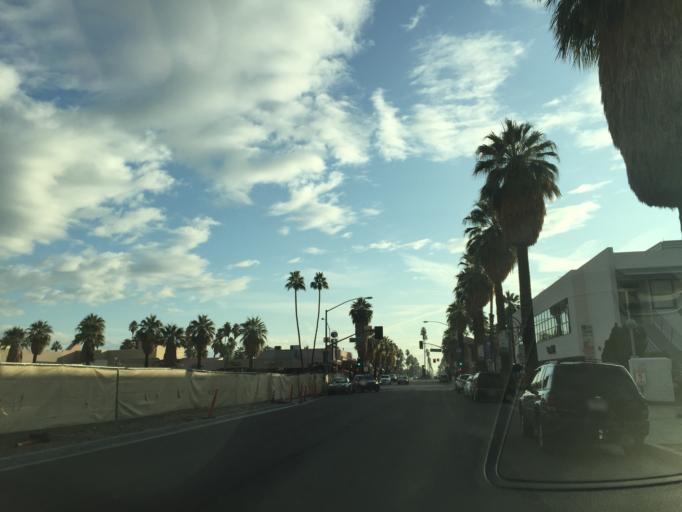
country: US
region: California
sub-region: Riverside County
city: Palm Springs
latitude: 33.8231
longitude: -116.5478
